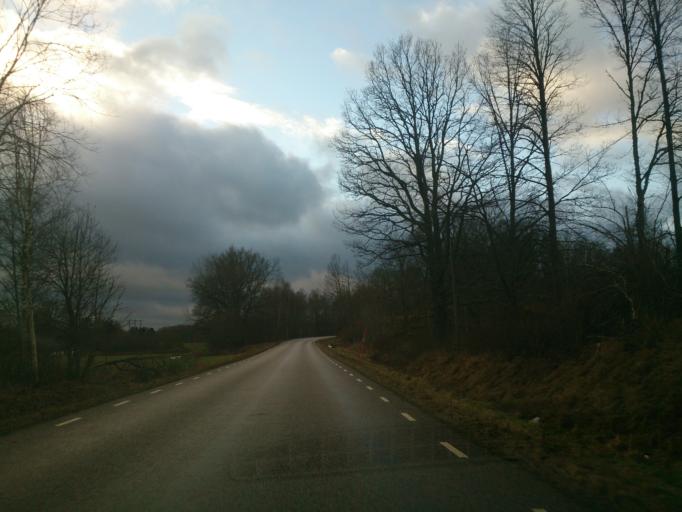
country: SE
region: OEstergoetland
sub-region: Atvidabergs Kommun
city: Atvidaberg
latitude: 58.2278
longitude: 15.9942
